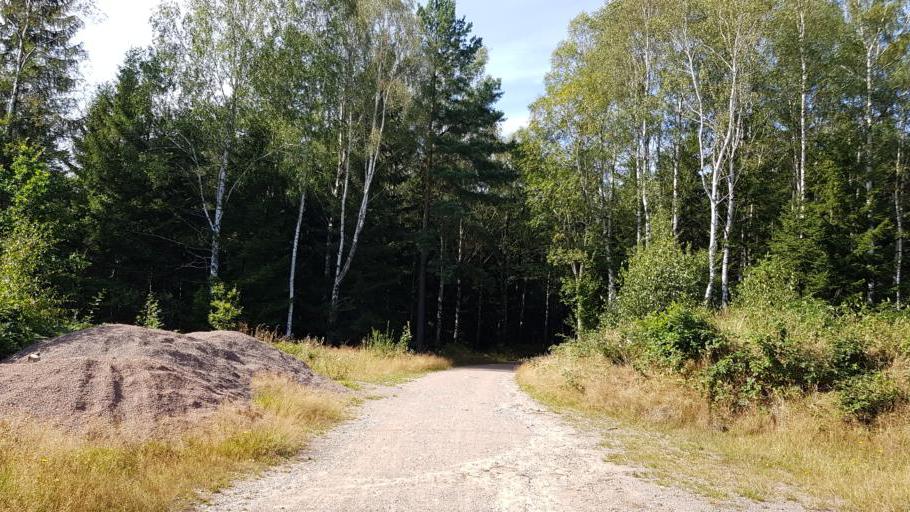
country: SE
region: Vaestra Goetaland
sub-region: Harryda Kommun
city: Molnlycke
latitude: 57.6776
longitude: 12.0701
